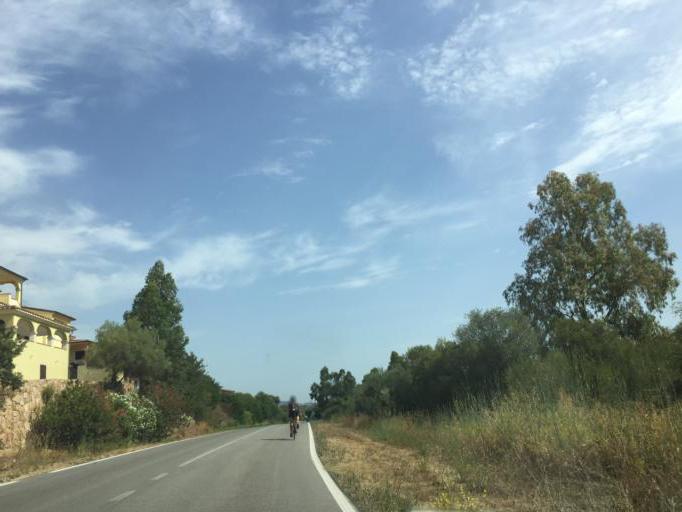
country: IT
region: Sardinia
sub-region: Provincia di Olbia-Tempio
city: San Teodoro
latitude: 40.7400
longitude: 9.6461
